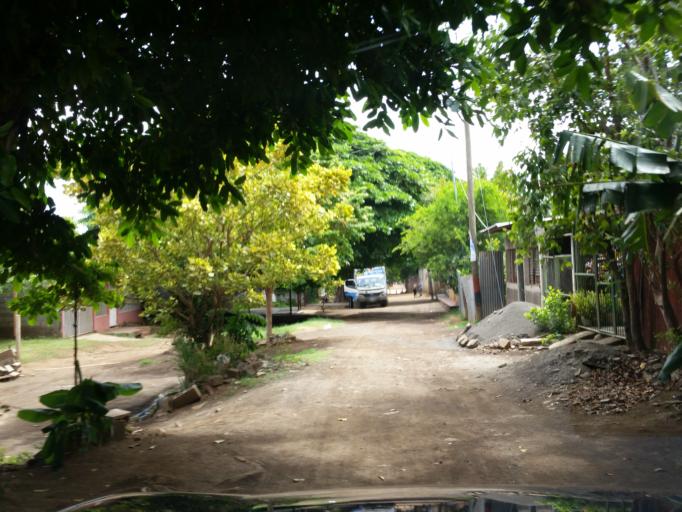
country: NI
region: Managua
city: Managua
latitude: 12.1326
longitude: -86.2834
